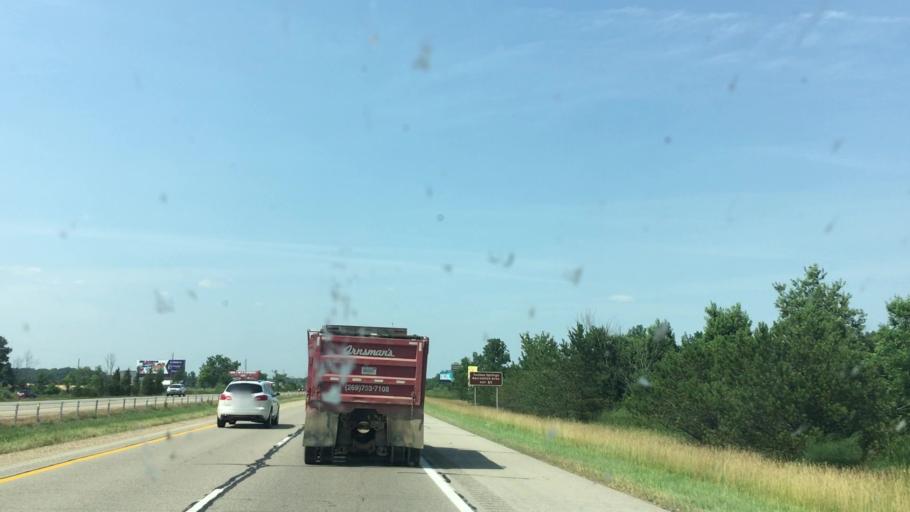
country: US
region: Michigan
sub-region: Allegan County
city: Wayland
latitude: 42.6208
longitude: -85.6622
